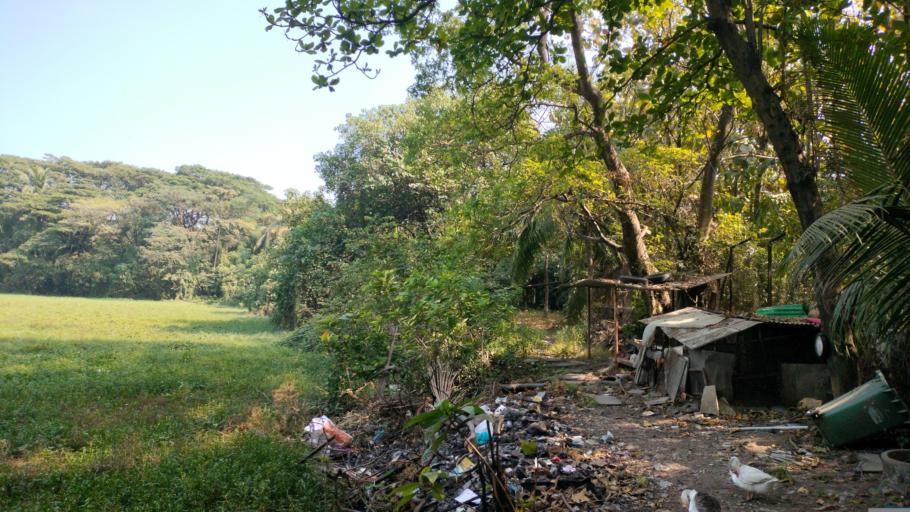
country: IN
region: Maharashtra
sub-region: Thane
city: Navi Mumbai
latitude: 19.0343
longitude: 72.9452
